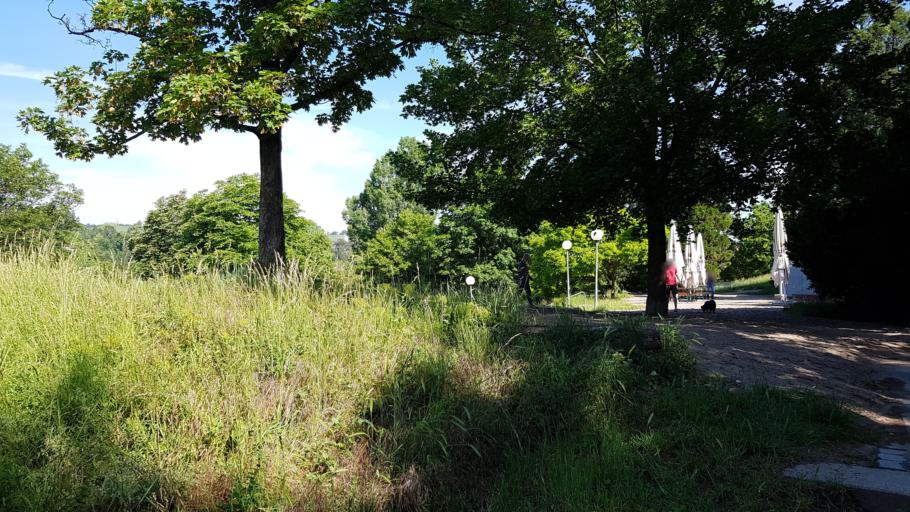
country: DE
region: Baden-Wuerttemberg
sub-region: Regierungsbezirk Stuttgart
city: Stuttgart-Ost
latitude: 48.8025
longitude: 9.2107
